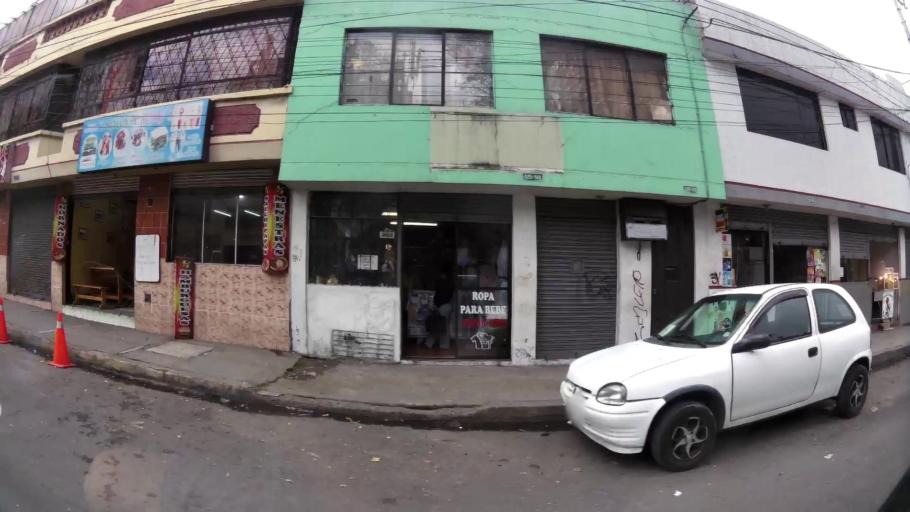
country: EC
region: Pichincha
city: Quito
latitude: -0.2736
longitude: -78.5437
